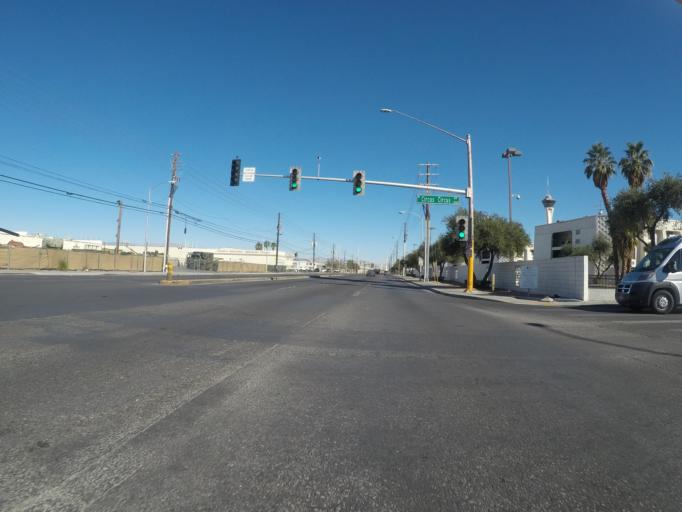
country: US
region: Nevada
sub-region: Clark County
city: Las Vegas
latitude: 36.1393
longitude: -115.1678
